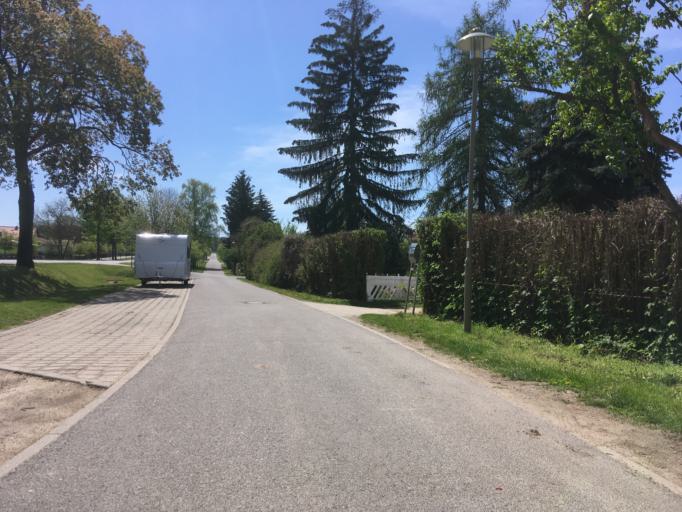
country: DE
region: Brandenburg
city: Wildau
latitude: 52.3358
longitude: 13.6087
